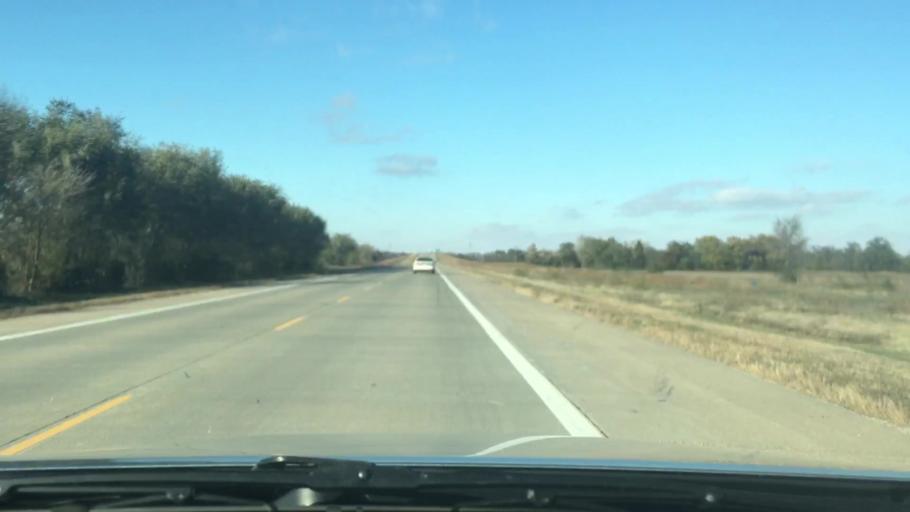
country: US
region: Kansas
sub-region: Reno County
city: Hutchinson
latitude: 38.0732
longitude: -97.9876
